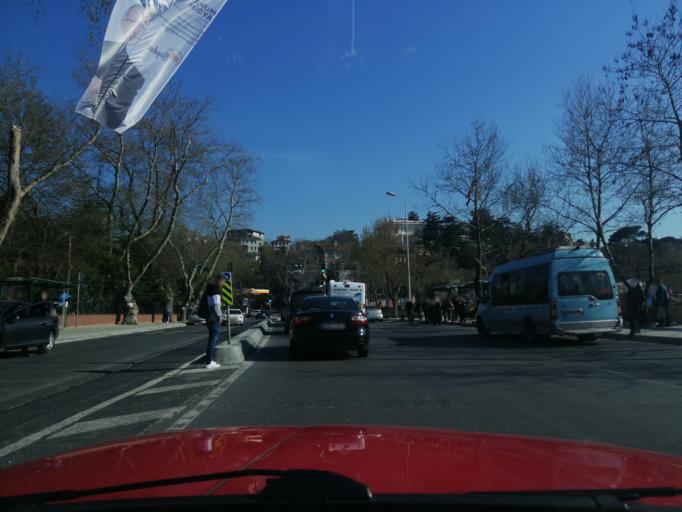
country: TR
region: Istanbul
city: UEskuedar
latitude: 41.0809
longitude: 29.0689
